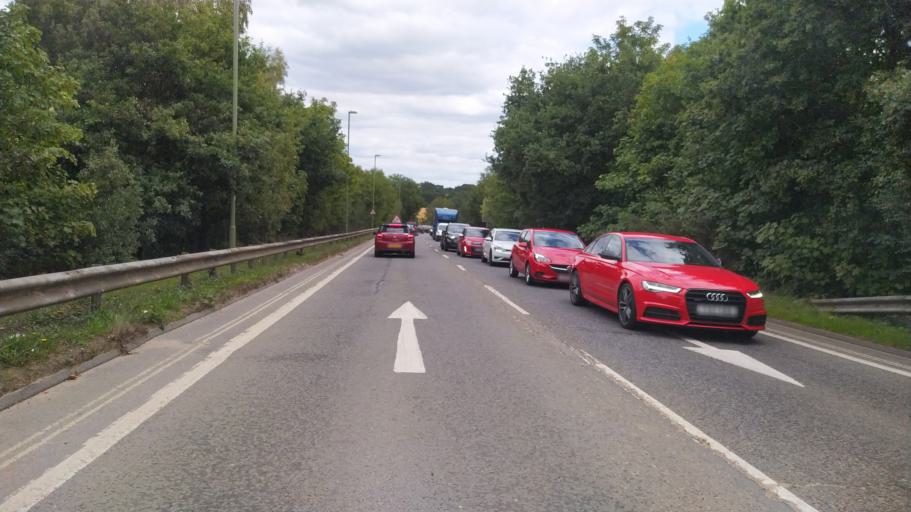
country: GB
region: England
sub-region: Hampshire
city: West End
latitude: 50.9157
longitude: -1.3254
